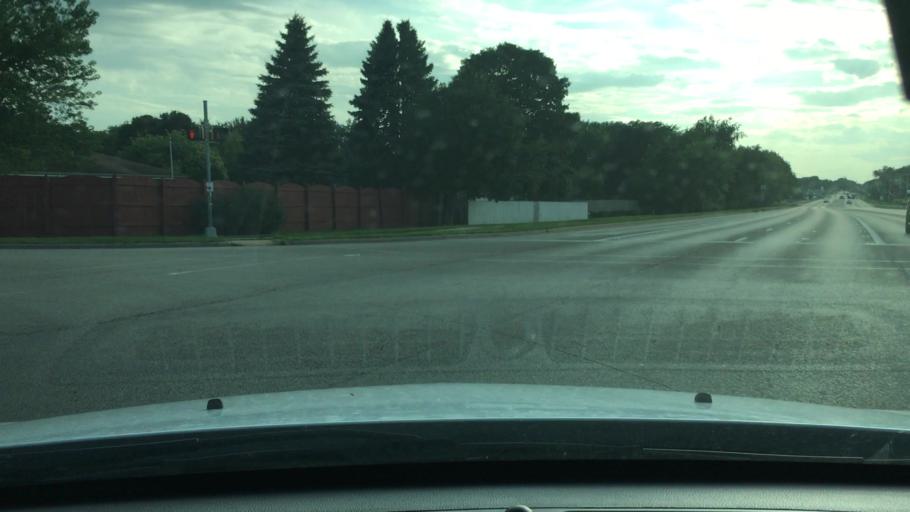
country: US
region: Illinois
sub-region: Ogle County
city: Rochelle
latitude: 41.9342
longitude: -89.0545
